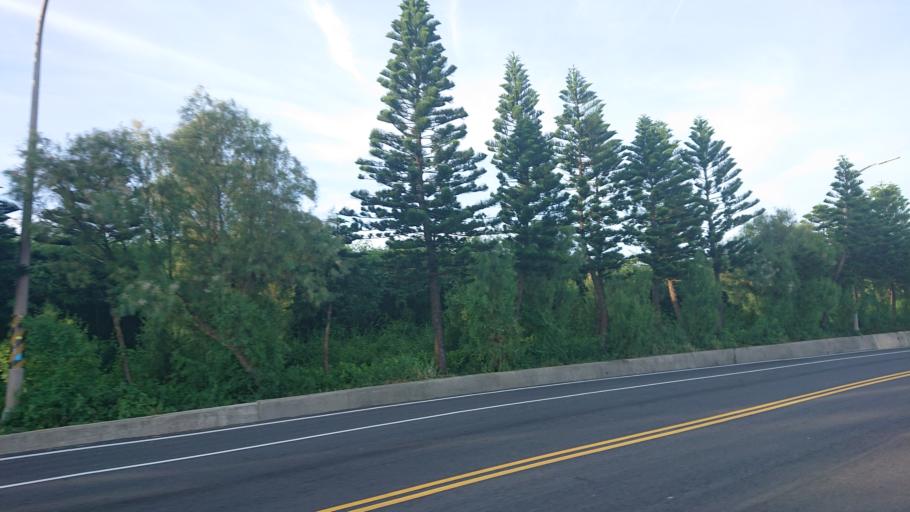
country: TW
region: Taiwan
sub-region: Penghu
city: Ma-kung
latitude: 23.6629
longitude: 119.5727
